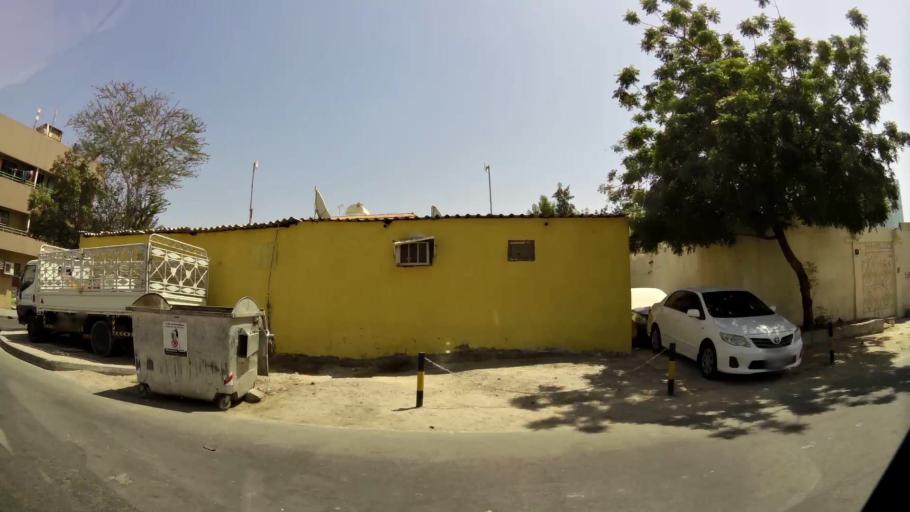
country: AE
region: Ash Shariqah
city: Sharjah
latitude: 25.2286
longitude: 55.2765
